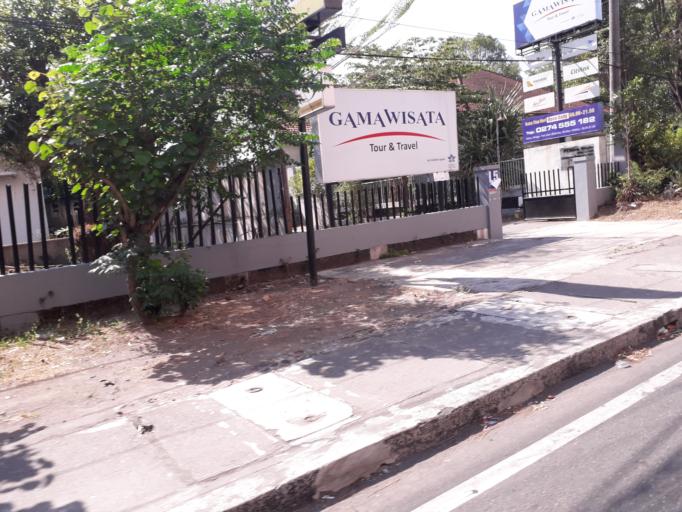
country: ID
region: Daerah Istimewa Yogyakarta
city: Yogyakarta
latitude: -7.7734
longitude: 110.3755
